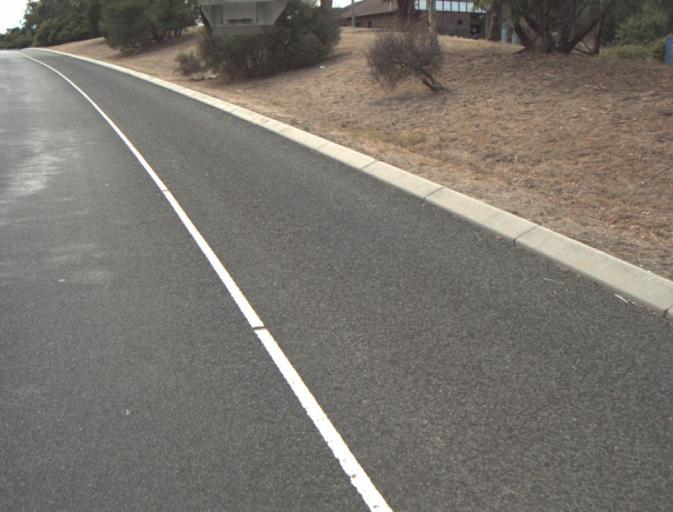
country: AU
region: Tasmania
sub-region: Launceston
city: Newnham
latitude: -41.3964
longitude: 147.1229
